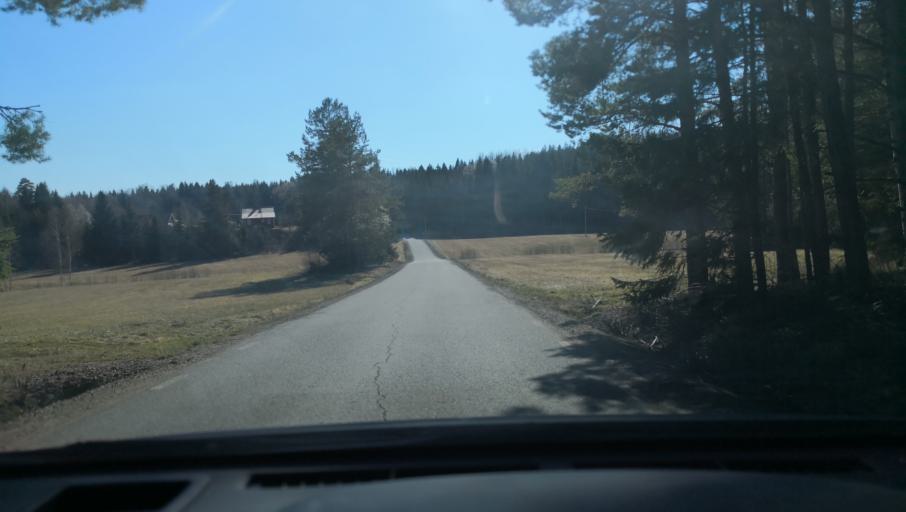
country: SE
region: Dalarna
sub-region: Avesta Kommun
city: Horndal
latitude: 60.0862
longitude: 16.4009
